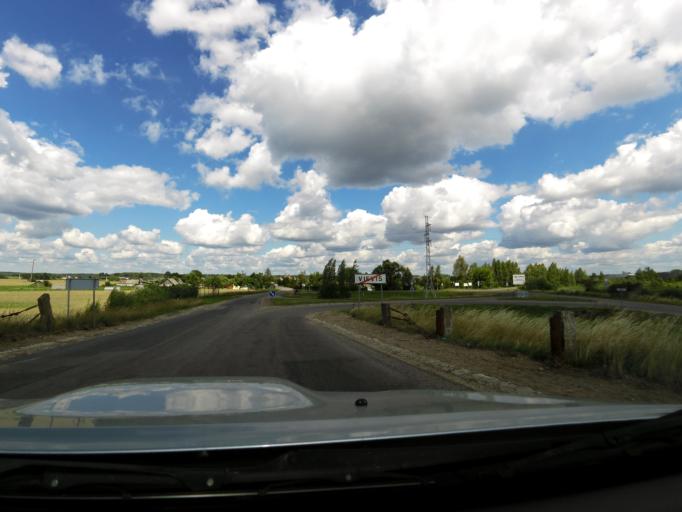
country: LT
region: Vilnius County
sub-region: Vilniaus Rajonas
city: Vievis
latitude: 54.7842
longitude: 24.8078
